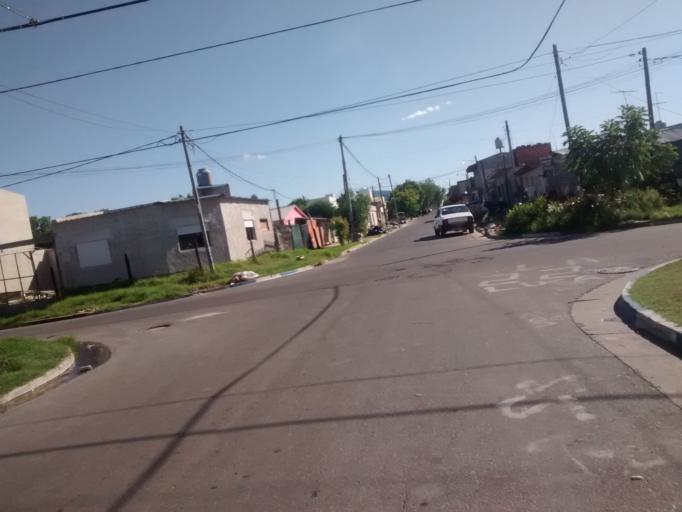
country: AR
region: Buenos Aires
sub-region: Partido de La Plata
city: La Plata
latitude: -34.9262
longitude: -57.9155
